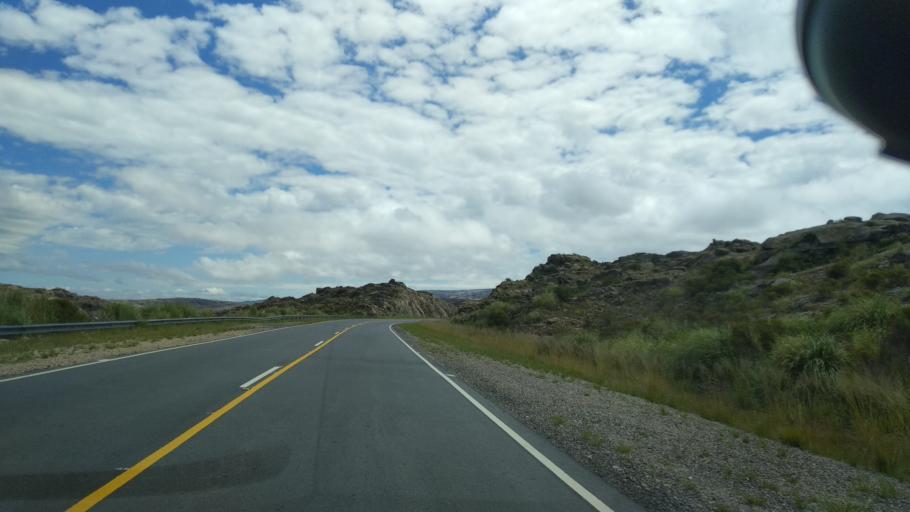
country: AR
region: Cordoba
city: Mina Clavero
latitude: -31.7256
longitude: -64.9013
